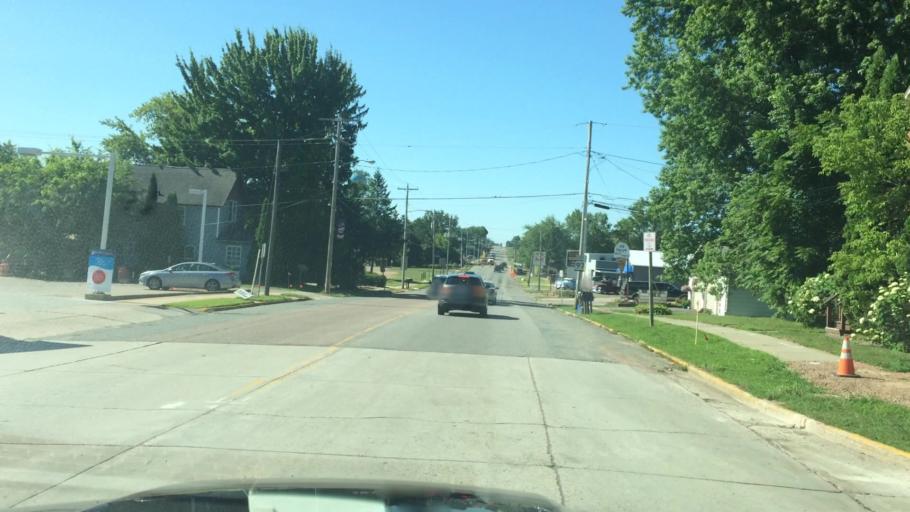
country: US
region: Wisconsin
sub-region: Marathon County
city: Stratford
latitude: 44.8008
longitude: -90.0792
